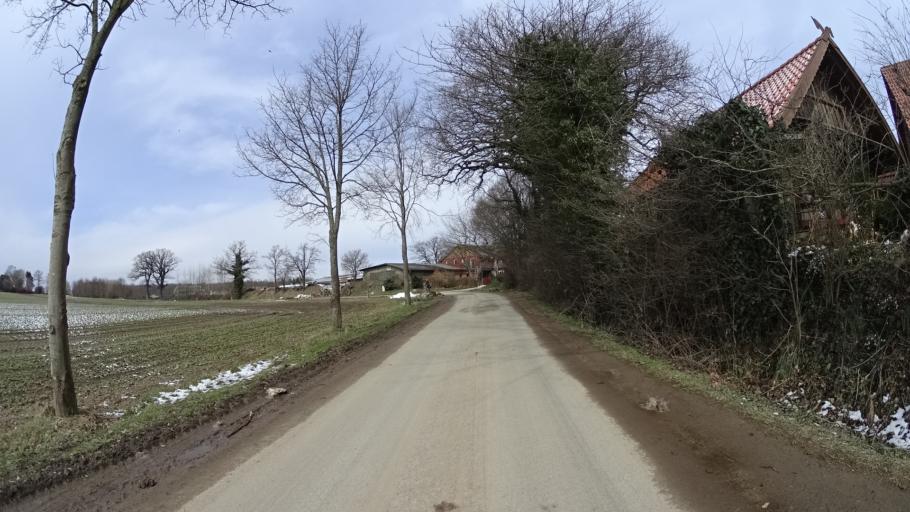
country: DE
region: Schleswig-Holstein
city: Rendswuhren
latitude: 54.0953
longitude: 10.1919
